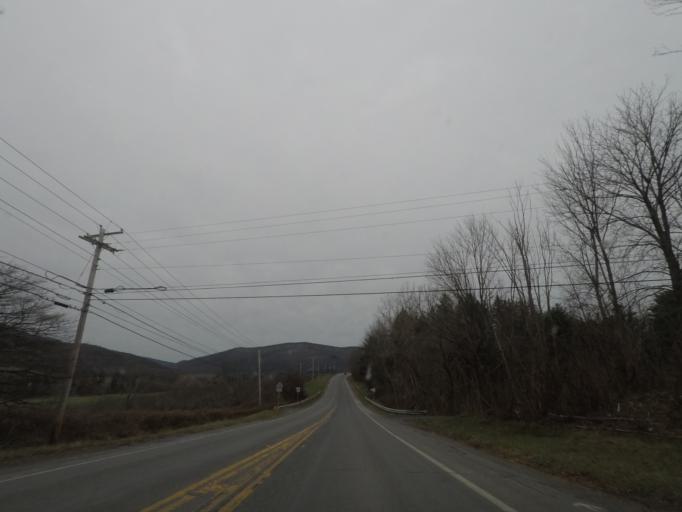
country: US
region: Massachusetts
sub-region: Berkshire County
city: Williamstown
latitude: 42.6697
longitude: -73.2380
